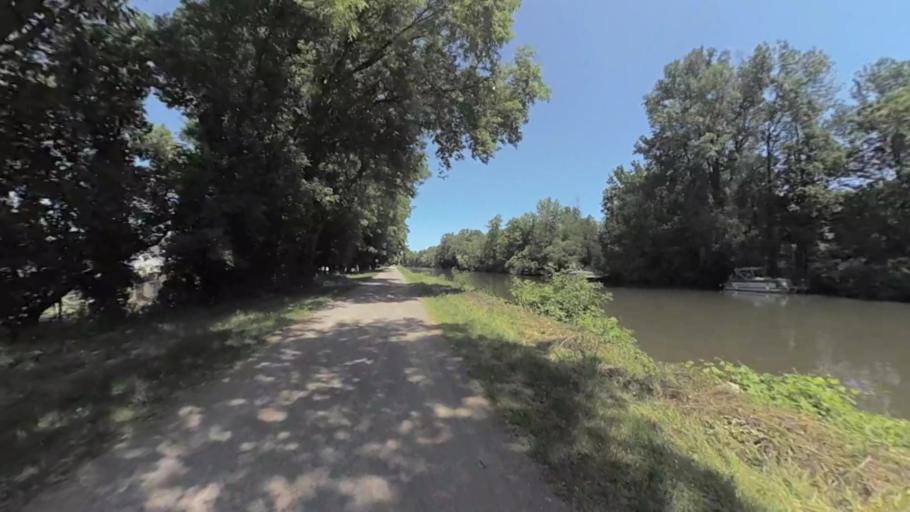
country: US
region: New York
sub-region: Monroe County
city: Fairport
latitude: 43.0942
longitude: -77.4558
